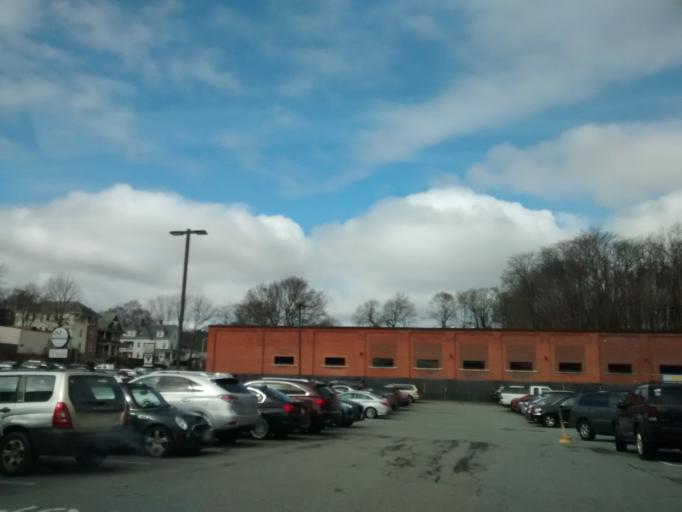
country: US
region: Massachusetts
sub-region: Worcester County
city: Worcester
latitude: 42.2892
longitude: -71.8078
